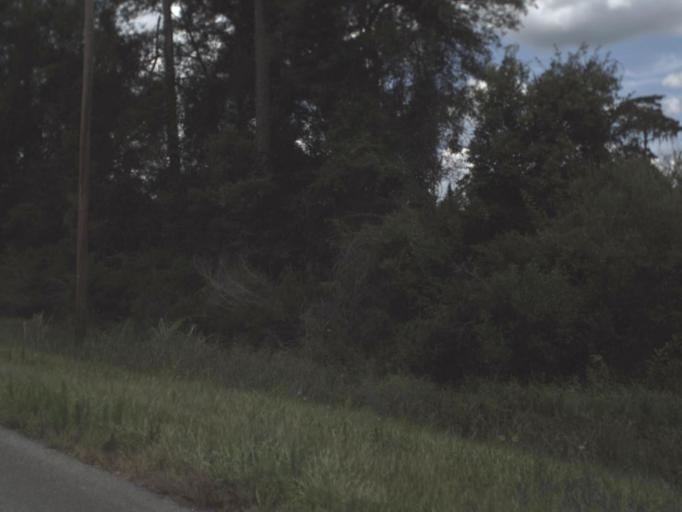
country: US
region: Florida
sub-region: Taylor County
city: Perry
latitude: 30.1003
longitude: -83.6958
